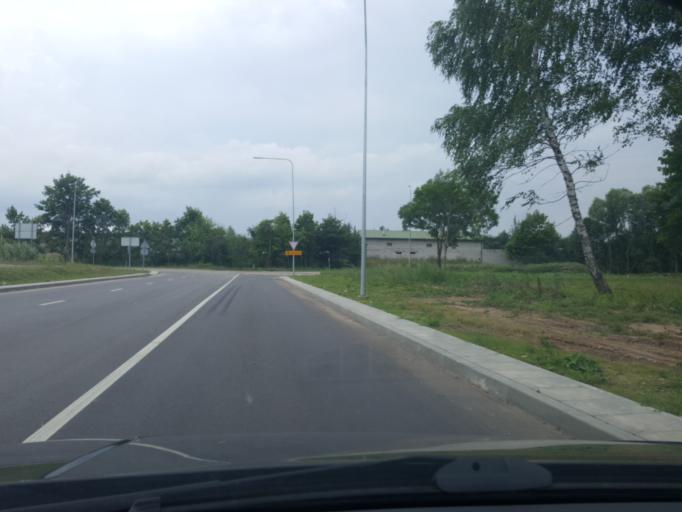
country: LT
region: Alytaus apskritis
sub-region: Alytus
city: Alytus
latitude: 54.4382
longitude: 24.0077
